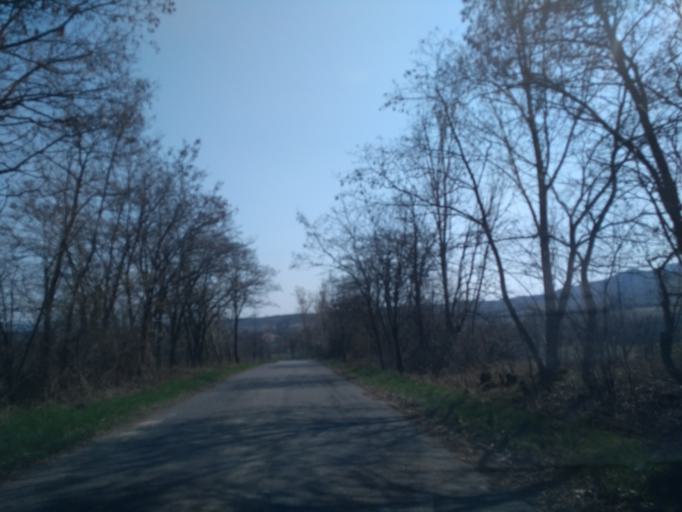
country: SK
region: Presovsky
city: Vranov nad Topl'ou
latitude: 48.8085
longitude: 21.6388
